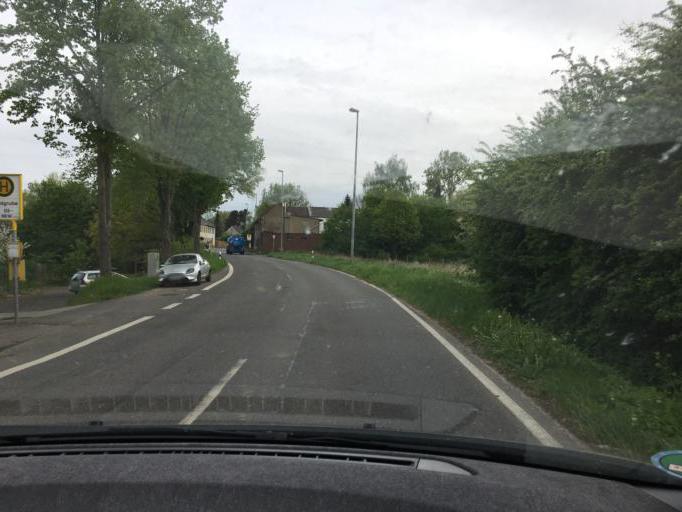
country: DE
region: North Rhine-Westphalia
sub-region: Regierungsbezirk Dusseldorf
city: Juchen
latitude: 51.1053
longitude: 6.4189
